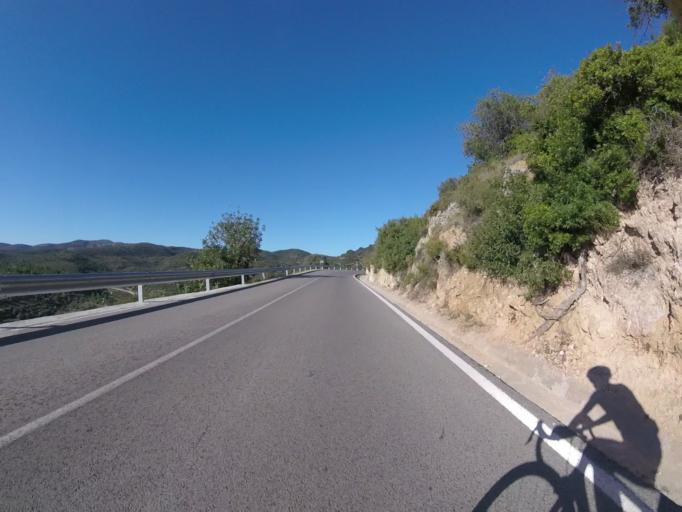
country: ES
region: Valencia
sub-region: Provincia de Castello
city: Cervera del Maestre
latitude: 40.4566
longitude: 0.2676
